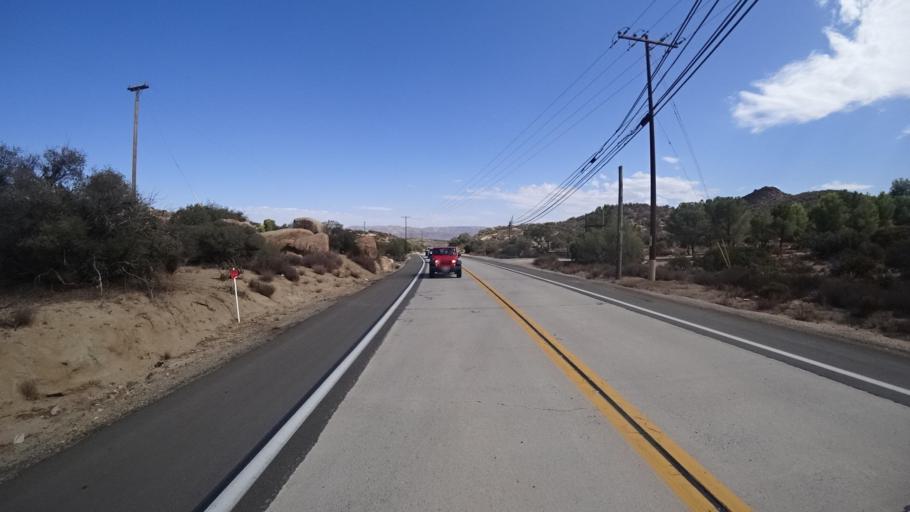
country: MX
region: Baja California
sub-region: Tecate
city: Cereso del Hongo
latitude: 32.6437
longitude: -116.2335
